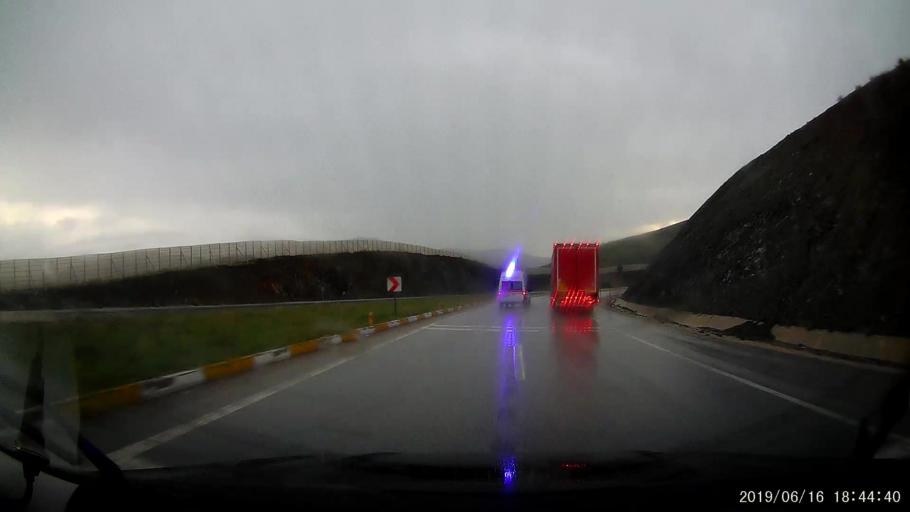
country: TR
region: Erzincan
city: Doganbeyli
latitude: 39.8695
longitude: 39.0681
